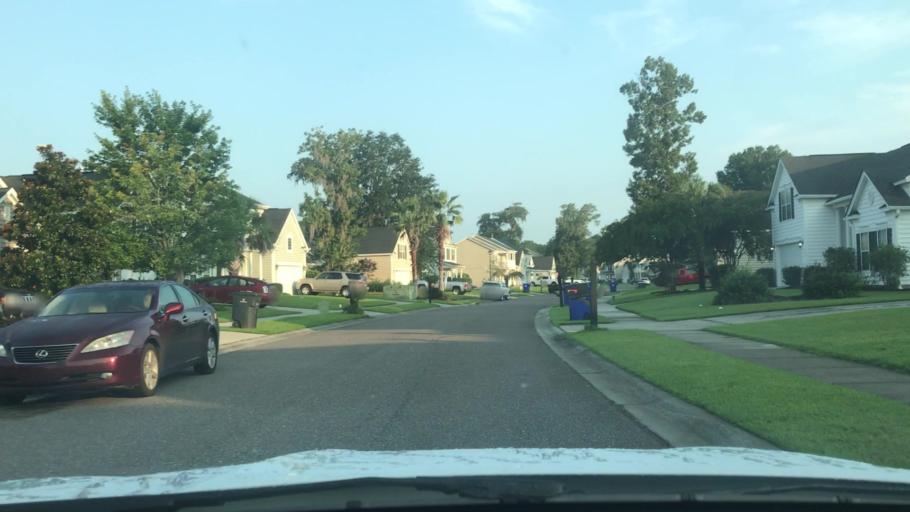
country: US
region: South Carolina
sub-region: Charleston County
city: Shell Point
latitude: 32.8323
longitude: -80.0985
